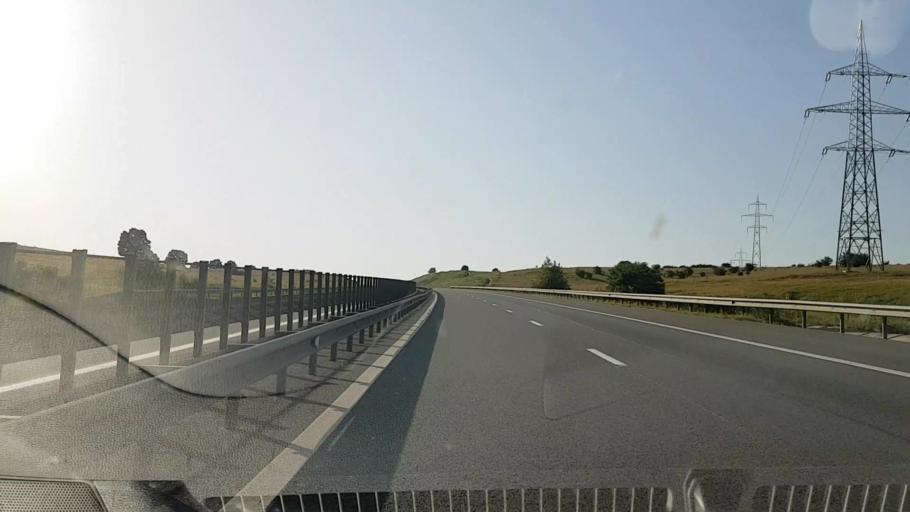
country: RO
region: Cluj
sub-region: Comuna Ciurila
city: Ciurila
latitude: 46.6506
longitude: 23.5110
